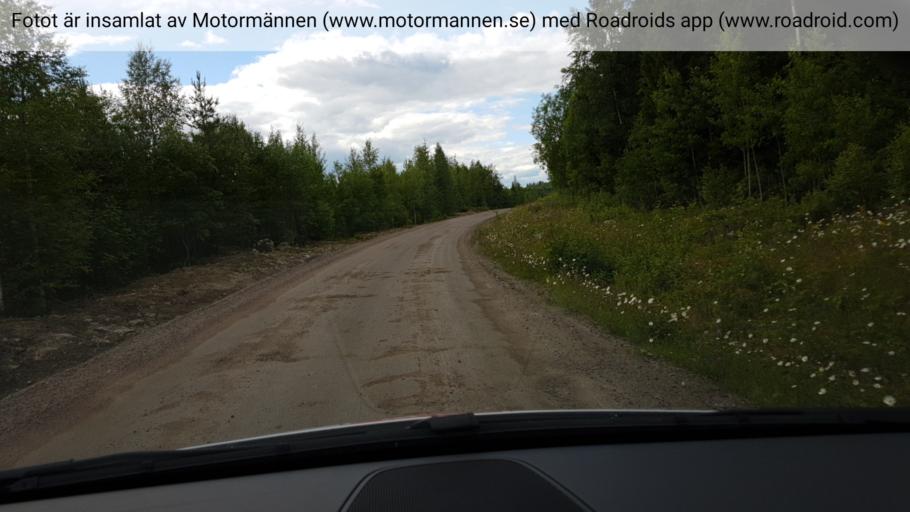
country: SE
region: Jaemtland
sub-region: Stroemsunds Kommun
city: Stroemsund
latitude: 64.0091
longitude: 15.9571
